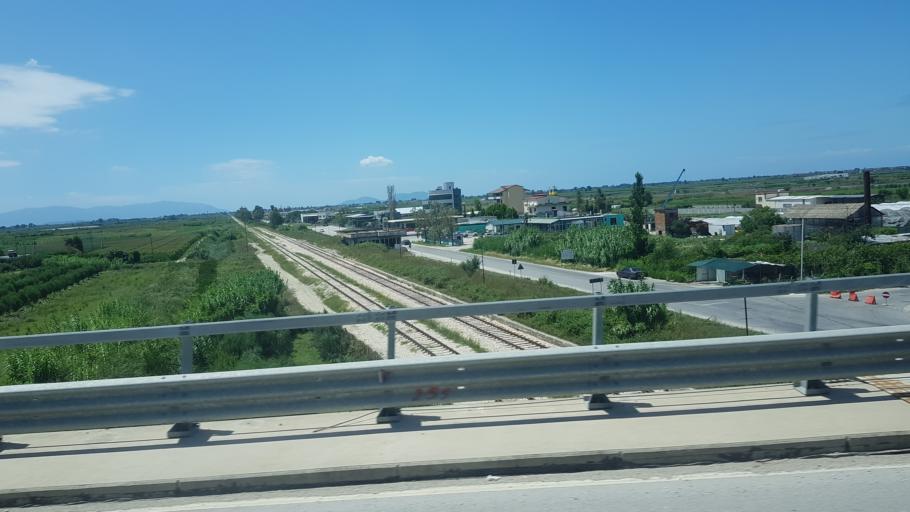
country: AL
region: Fier
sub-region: Rrethi i Fierit
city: Levan
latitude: 40.6691
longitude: 19.4851
